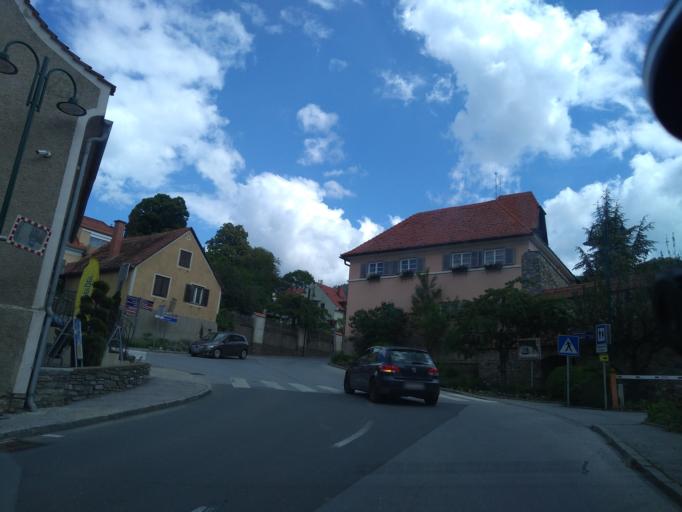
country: AT
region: Styria
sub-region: Politischer Bezirk Graz-Umgebung
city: Frohnleiten
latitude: 47.2708
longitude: 15.3239
